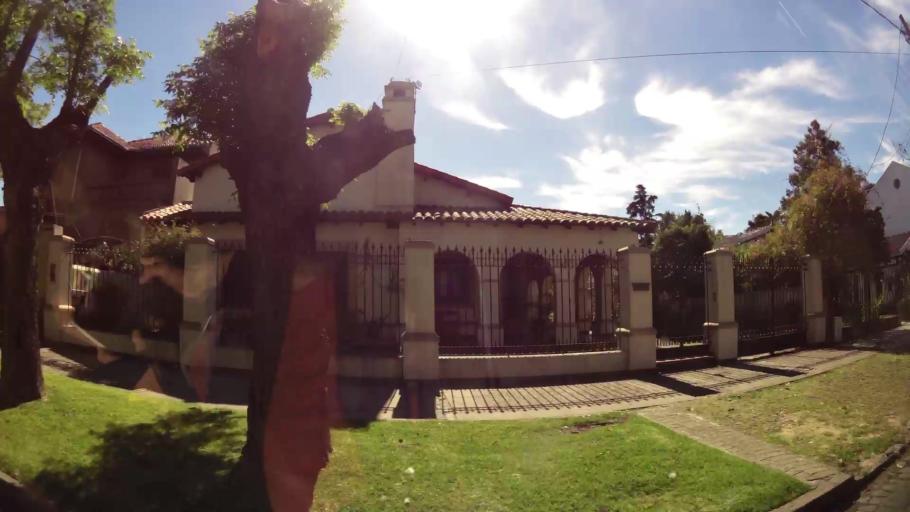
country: AR
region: Buenos Aires
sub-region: Partido de Lomas de Zamora
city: Lomas de Zamora
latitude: -34.7455
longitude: -58.4011
